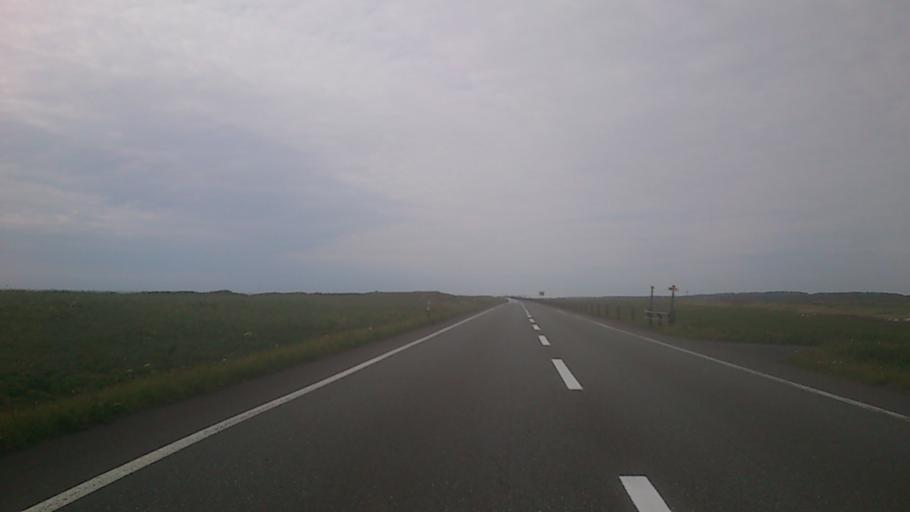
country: JP
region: Hokkaido
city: Wakkanai
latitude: 45.0603
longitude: 141.6471
